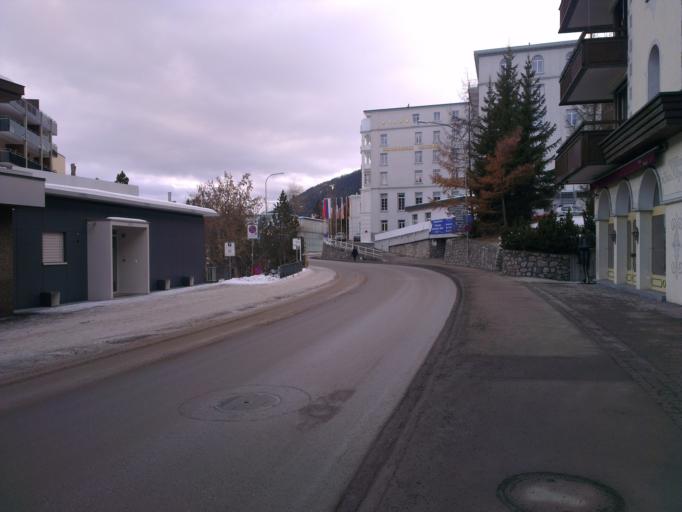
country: CH
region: Grisons
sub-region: Praettigau/Davos District
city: Davos
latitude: 46.8012
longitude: 9.8280
